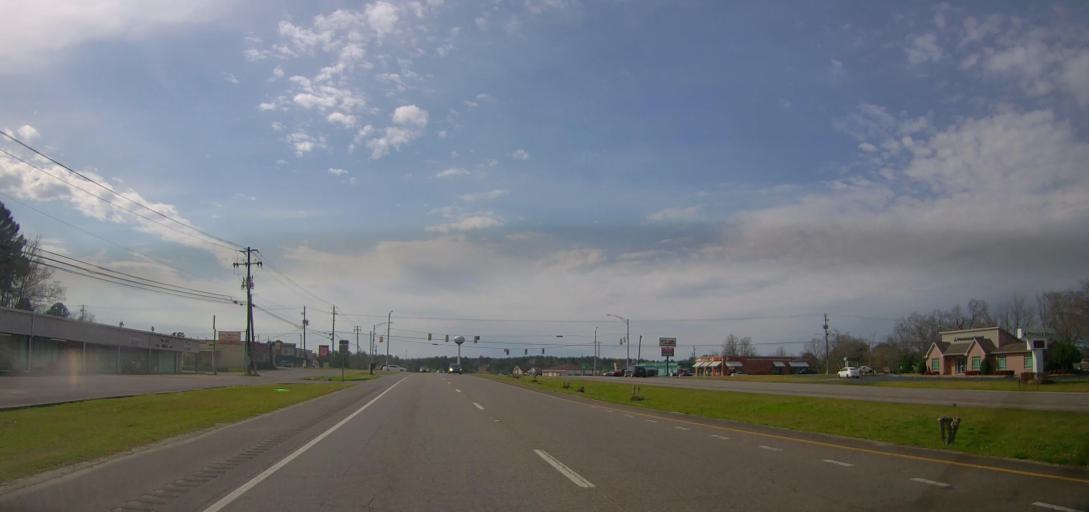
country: US
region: Alabama
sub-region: Walker County
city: Sumiton
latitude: 33.7437
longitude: -87.0439
